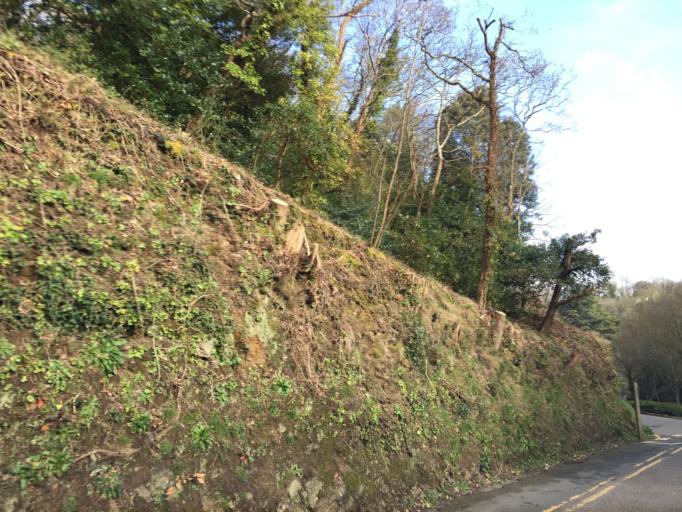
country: JE
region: St Helier
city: Saint Helier
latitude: 49.2099
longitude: -2.1540
